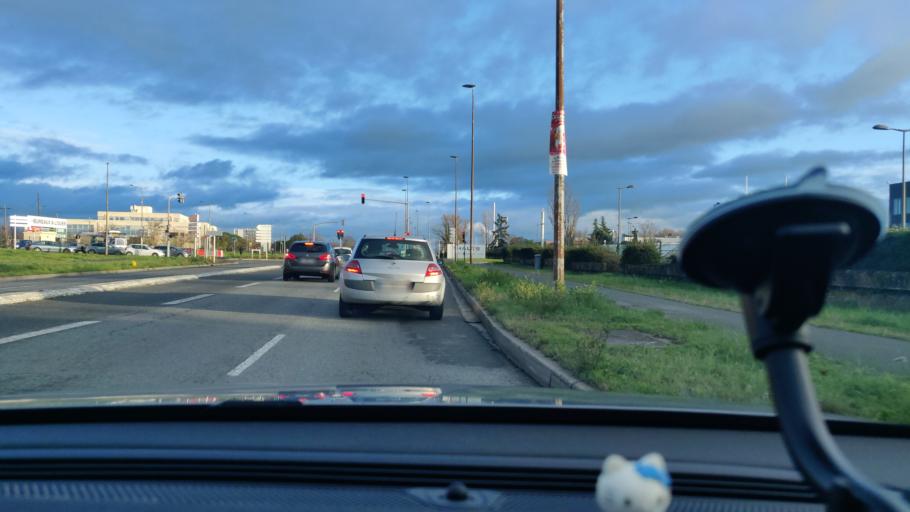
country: FR
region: Midi-Pyrenees
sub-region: Departement de la Haute-Garonne
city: Portet-sur-Garonne
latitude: 43.5652
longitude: 1.3829
